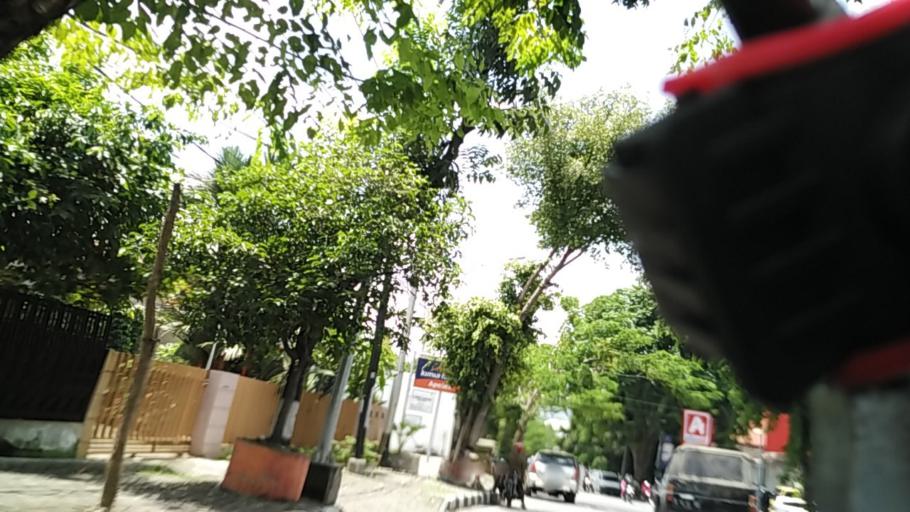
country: ID
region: Central Java
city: Semarang
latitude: -6.9912
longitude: 110.3815
